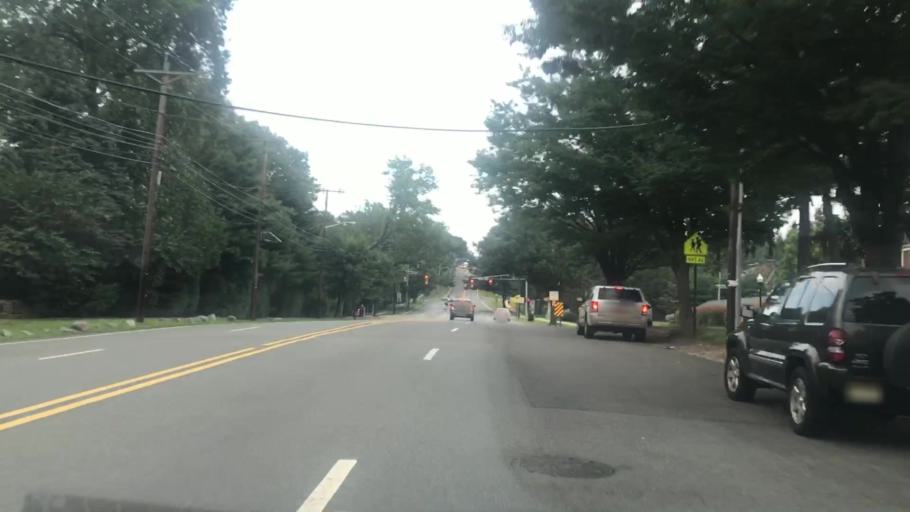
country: US
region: New Jersey
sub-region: Bergen County
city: Englewood
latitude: 40.8892
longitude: -73.9665
